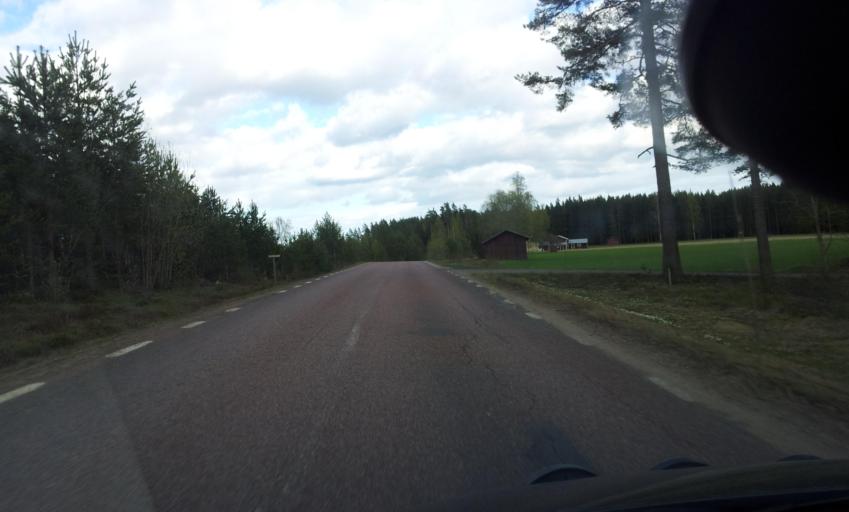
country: SE
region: Gaevleborg
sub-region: Bollnas Kommun
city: Arbra
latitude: 61.4232
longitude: 16.5225
